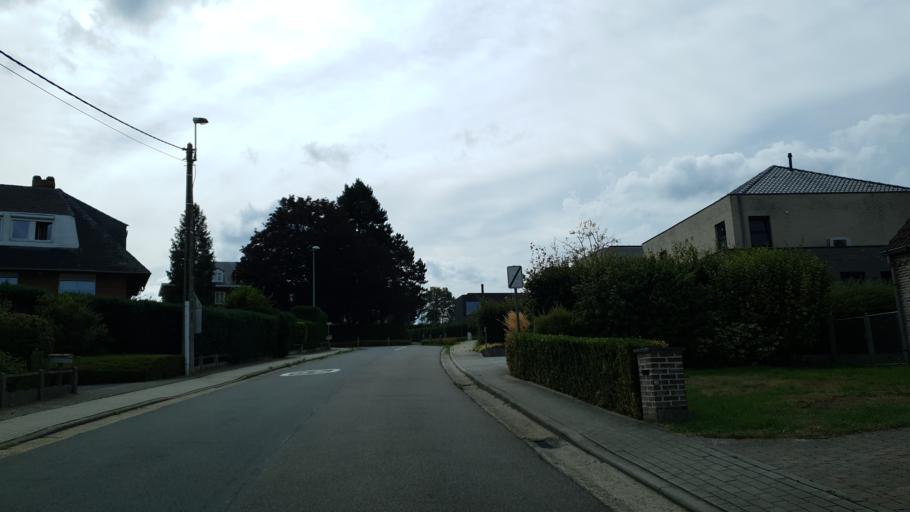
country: BE
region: Flanders
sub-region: Provincie Vlaams-Brabant
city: Herent
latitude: 50.8976
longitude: 4.6780
